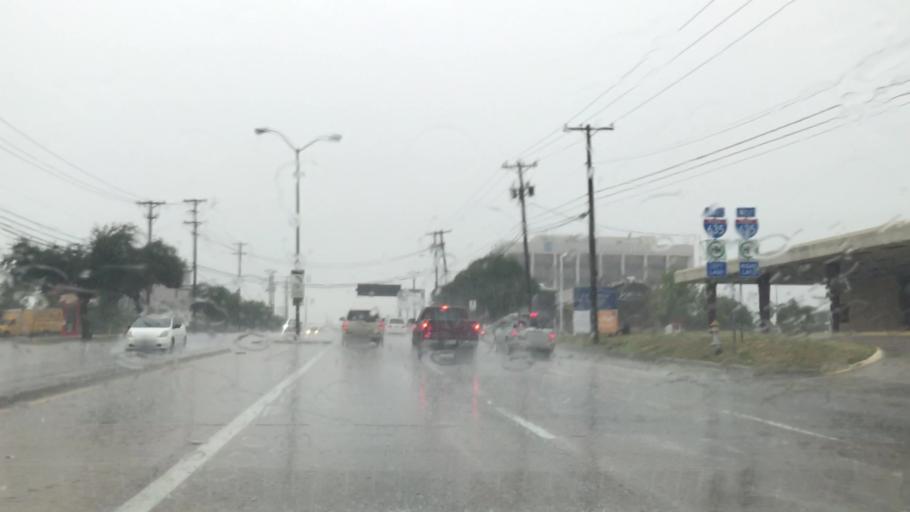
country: US
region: Texas
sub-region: Dallas County
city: Addison
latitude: 32.9290
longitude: -96.8034
